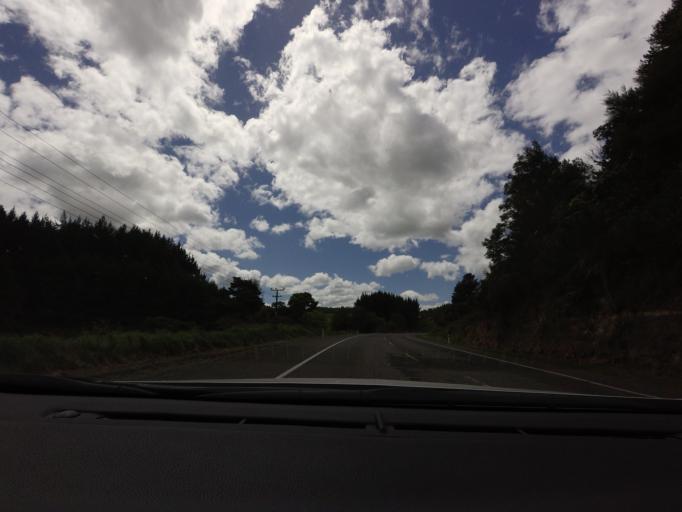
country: NZ
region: Bay of Plenty
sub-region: Rotorua District
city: Rotorua
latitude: -38.3269
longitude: 176.3693
